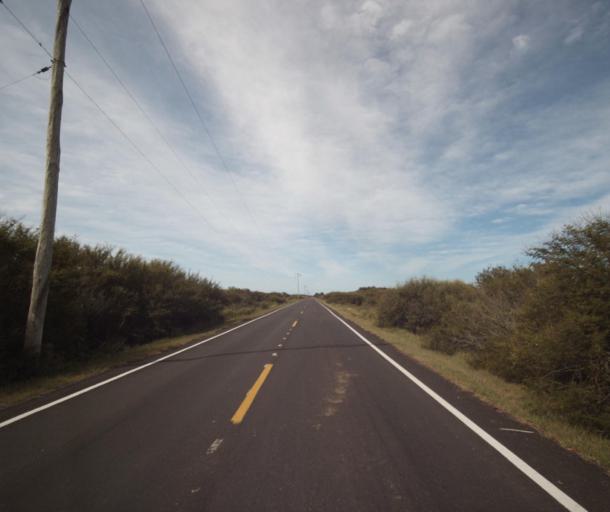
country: BR
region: Rio Grande do Sul
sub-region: Rio Grande
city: Rio Grande
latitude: -31.9126
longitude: -51.9372
